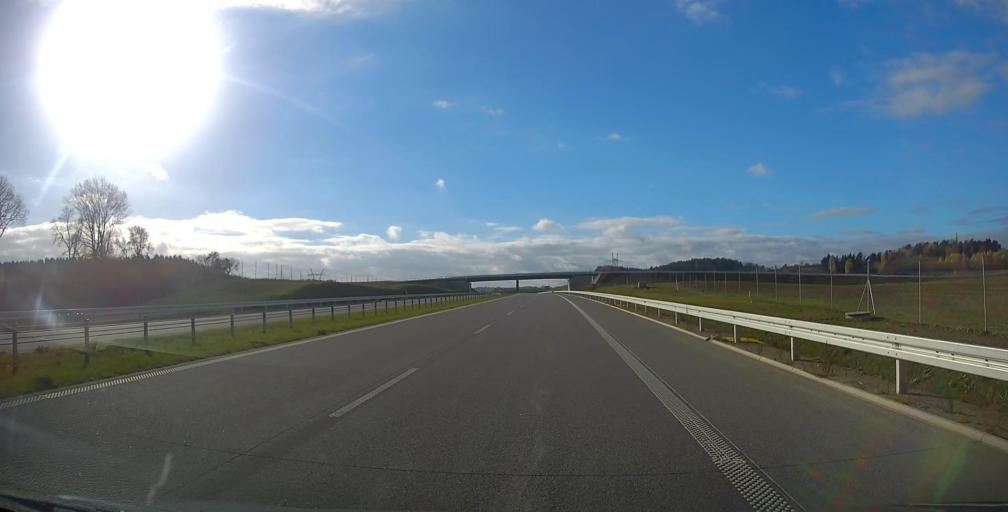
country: PL
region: Warmian-Masurian Voivodeship
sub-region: Powiat elcki
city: Elk
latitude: 53.7492
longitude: 22.3137
